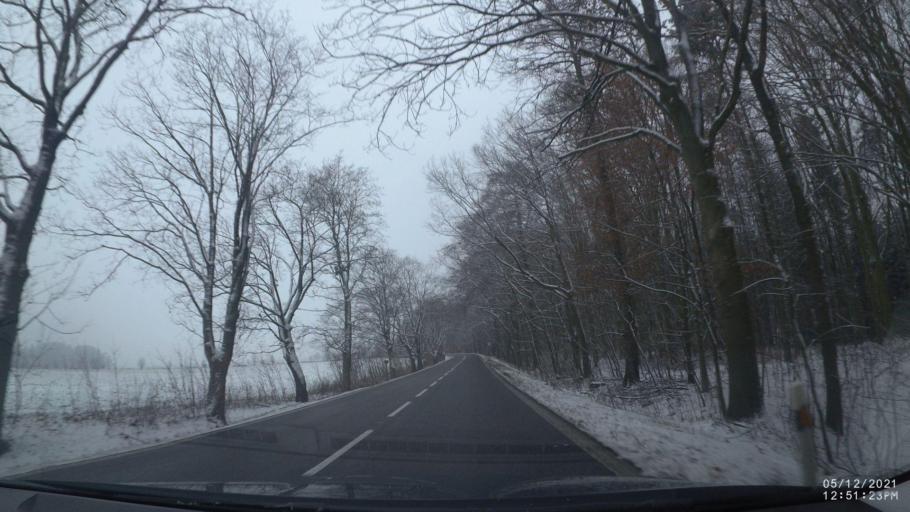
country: CZ
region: Kralovehradecky
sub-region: Okres Nachod
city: Nachod
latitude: 50.3962
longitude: 16.1387
